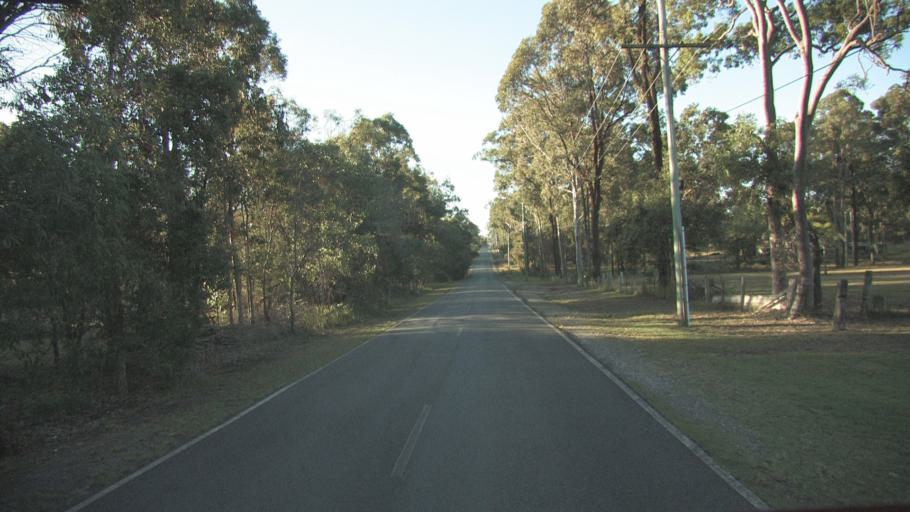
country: AU
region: Queensland
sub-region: Logan
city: Waterford West
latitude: -27.7254
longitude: 153.1413
